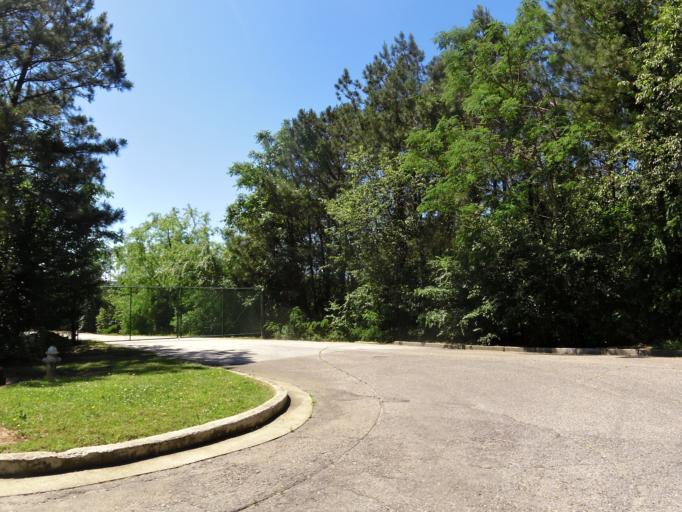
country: US
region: Georgia
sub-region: Columbia County
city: Martinez
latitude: 33.5079
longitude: -82.0323
